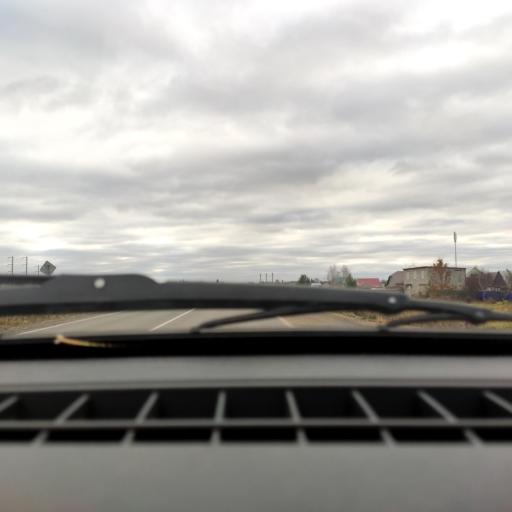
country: RU
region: Bashkortostan
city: Iglino
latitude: 54.7812
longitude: 56.2531
